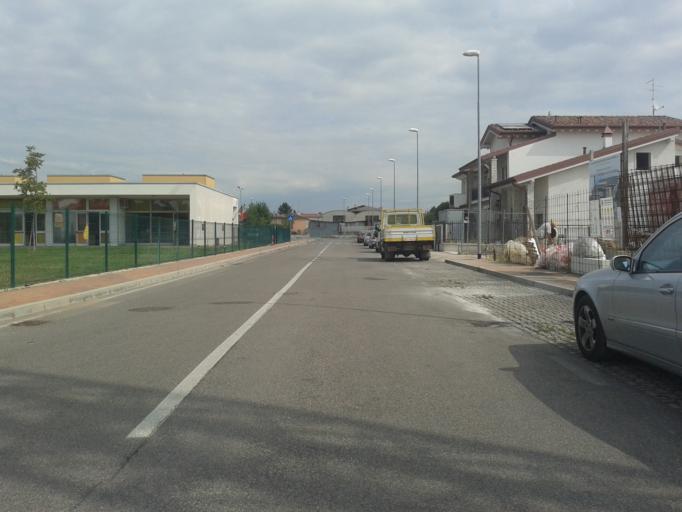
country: IT
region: Veneto
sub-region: Provincia di Verona
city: Mozzecane
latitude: 45.3080
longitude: 10.8125
